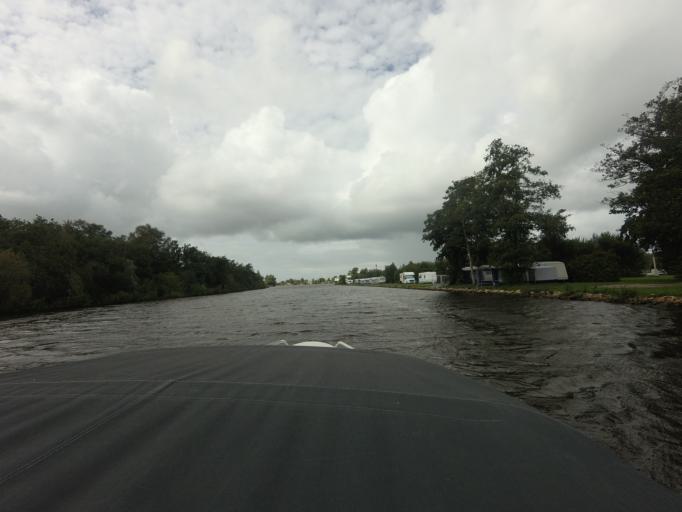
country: NL
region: Friesland
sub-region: Gemeente Boarnsterhim
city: Warten
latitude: 53.1258
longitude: 5.9379
